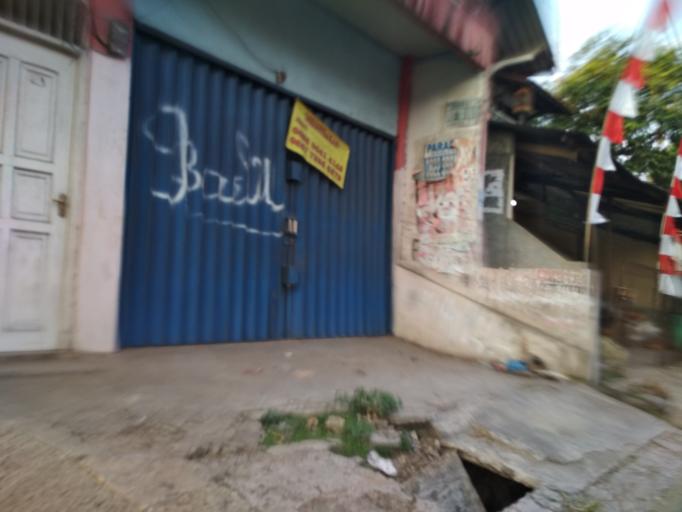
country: ID
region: West Java
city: Ciampea
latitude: -6.5629
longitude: 106.7212
